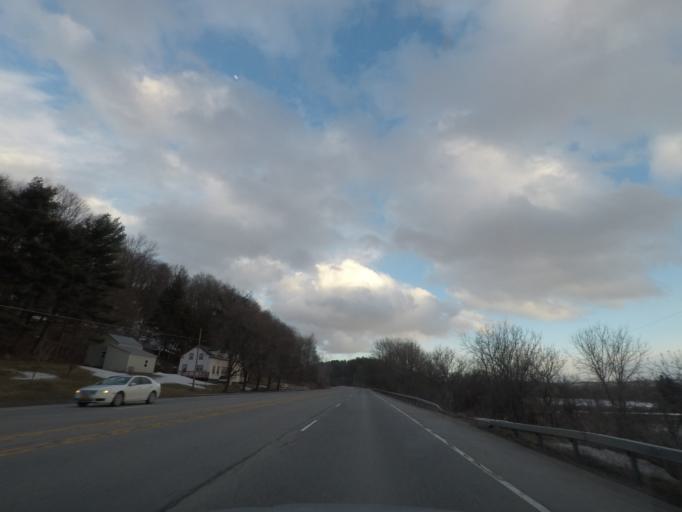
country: US
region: New York
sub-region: Herkimer County
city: Little Falls
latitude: 43.0279
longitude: -74.7941
